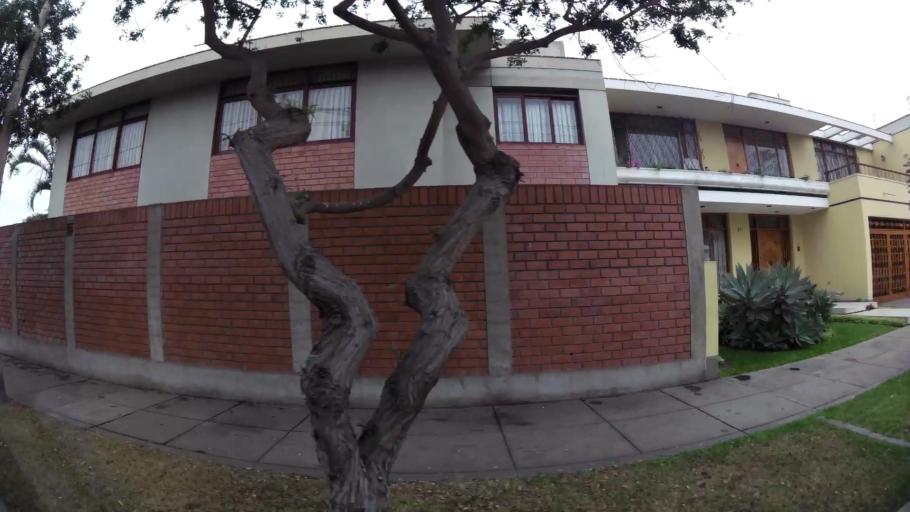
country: PE
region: Lima
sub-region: Lima
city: Surco
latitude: -12.1293
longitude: -77.0135
